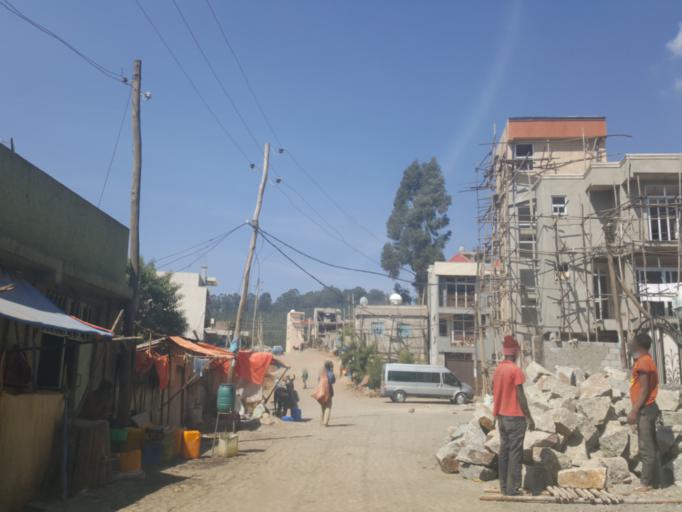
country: ET
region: Adis Abeba
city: Addis Ababa
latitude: 9.0705
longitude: 38.7180
